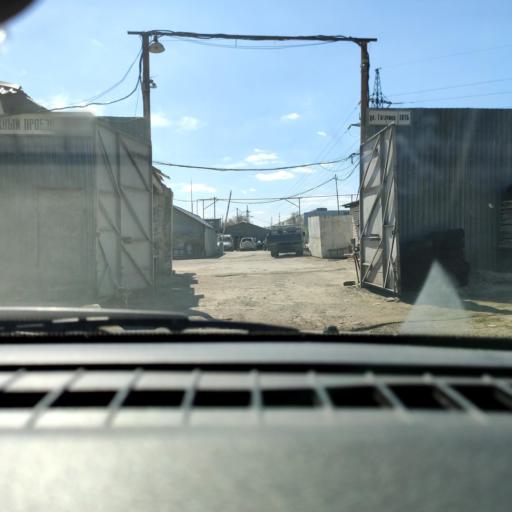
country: RU
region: Samara
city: Samara
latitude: 53.1997
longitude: 50.2368
